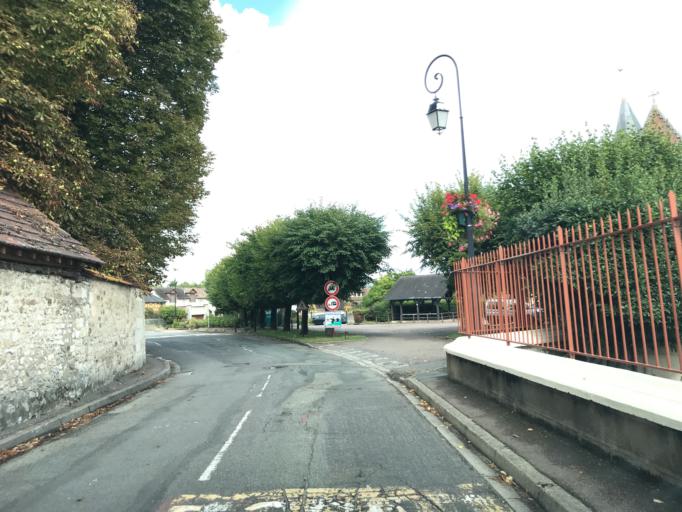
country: FR
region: Haute-Normandie
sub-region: Departement de l'Eure
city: Saint-Just
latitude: 49.1080
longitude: 1.4404
